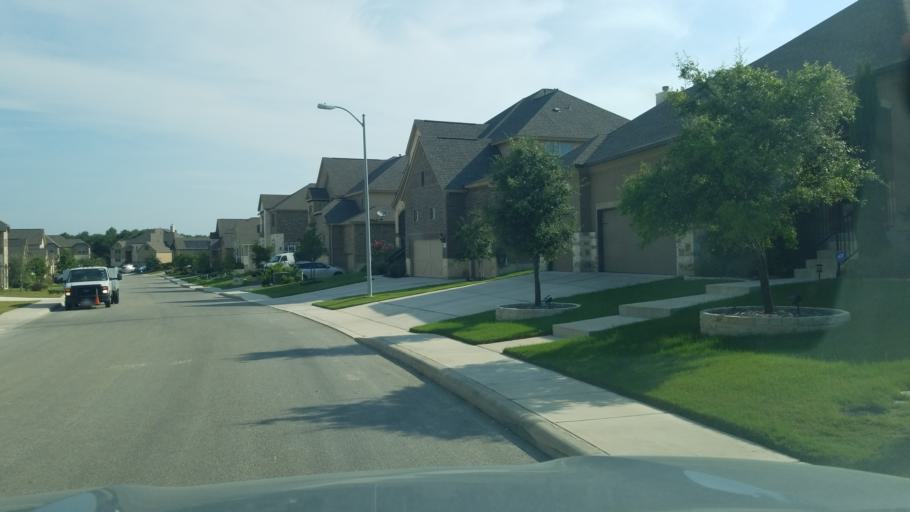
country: US
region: Texas
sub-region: Bexar County
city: Scenic Oaks
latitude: 29.6936
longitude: -98.6396
